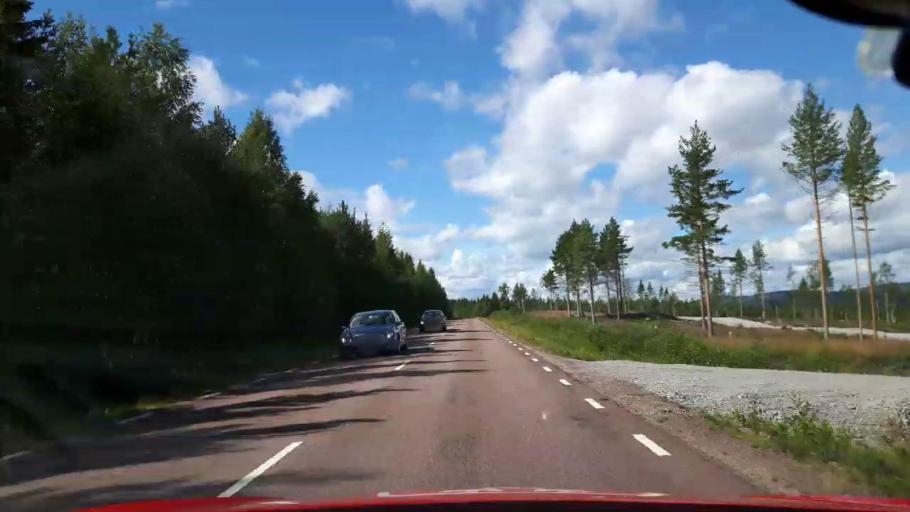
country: SE
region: Jaemtland
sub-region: Harjedalens Kommun
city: Sveg
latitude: 61.9958
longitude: 14.2387
